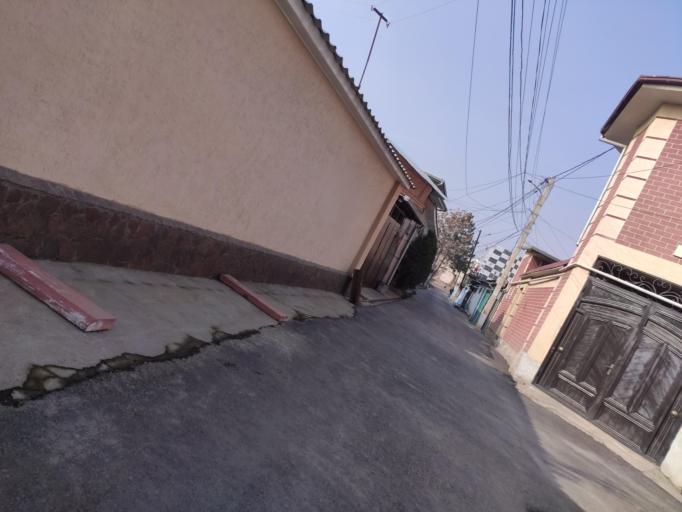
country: UZ
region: Toshkent Shahri
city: Tashkent
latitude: 41.2736
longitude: 69.2710
